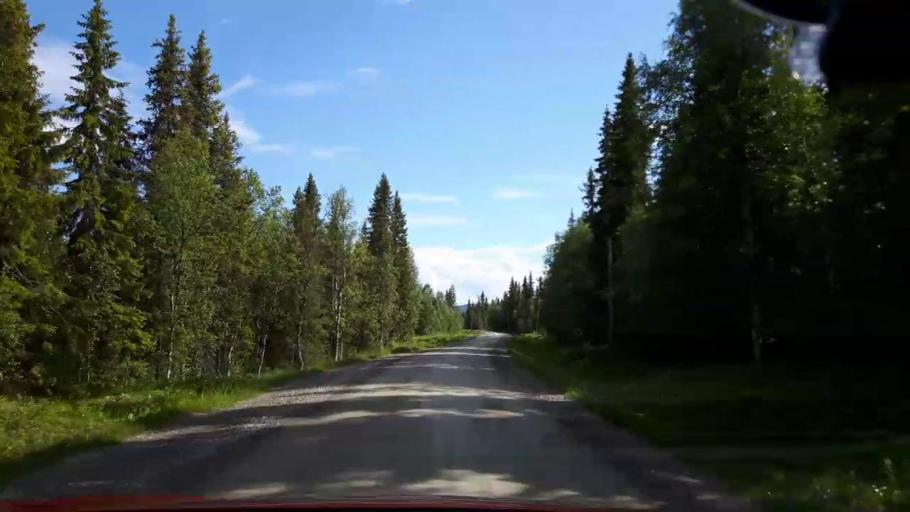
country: SE
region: Jaemtland
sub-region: Krokoms Kommun
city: Valla
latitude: 63.7941
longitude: 14.0468
